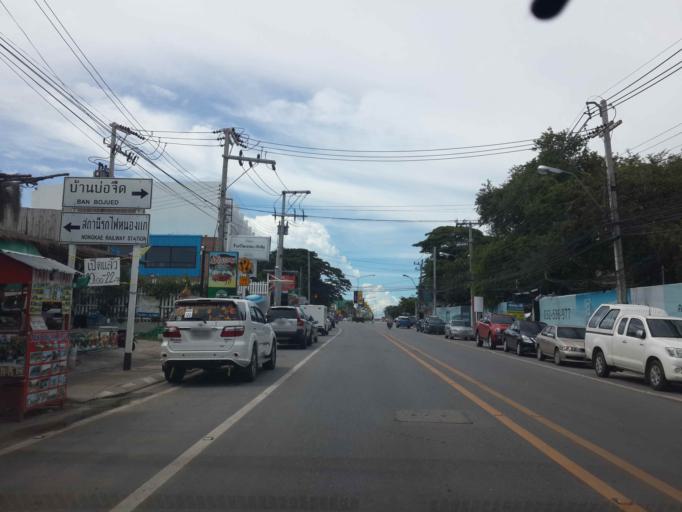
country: TH
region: Prachuap Khiri Khan
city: Hua Hin
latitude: 12.5326
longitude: 99.9659
